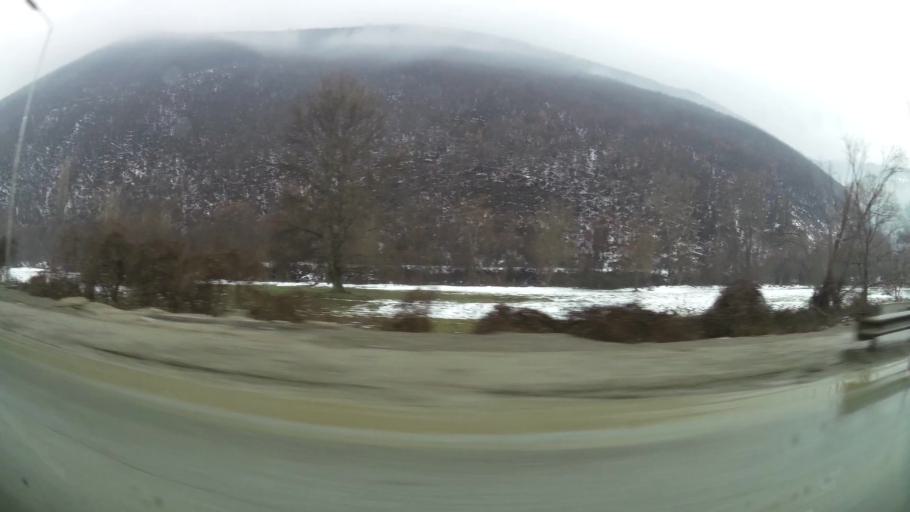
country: XK
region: Ferizaj
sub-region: Hani i Elezit
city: Hani i Elezit
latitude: 42.1599
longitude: 21.2855
